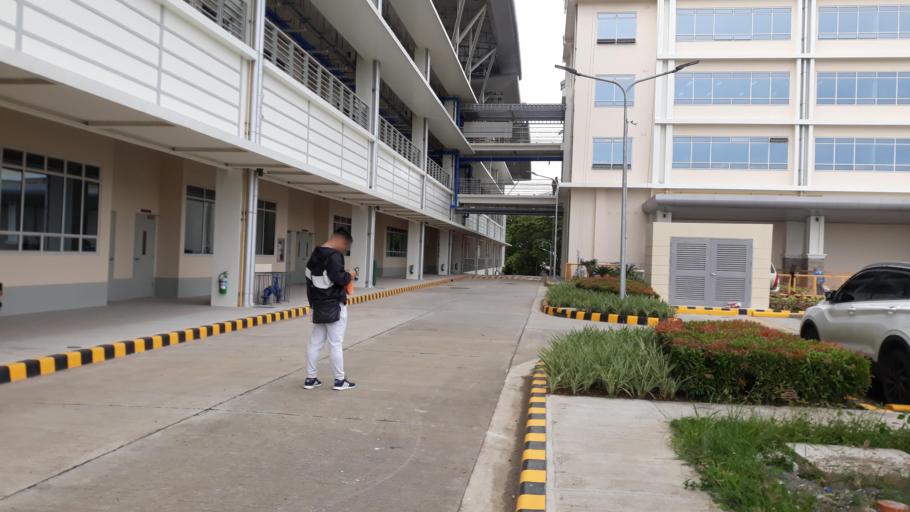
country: PH
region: Calabarzon
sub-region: Province of Cavite
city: Manggahan
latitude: 14.2890
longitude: 120.9148
